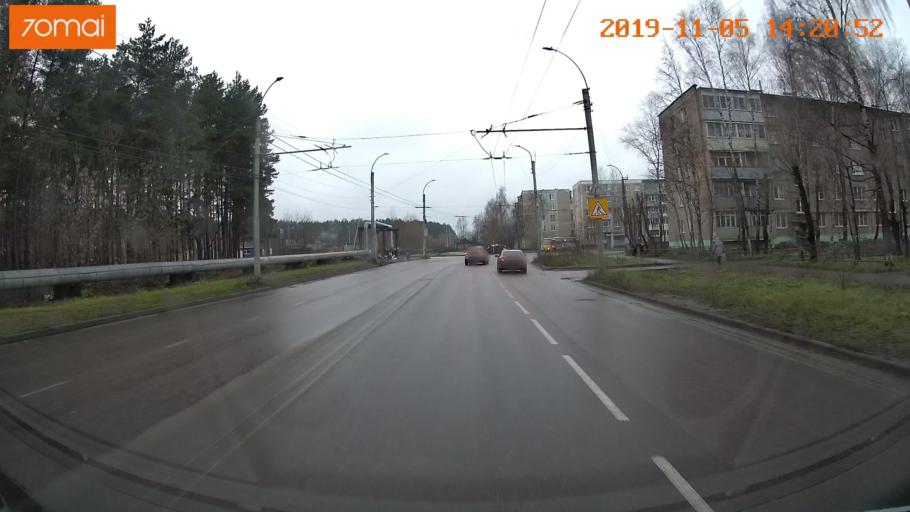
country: RU
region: Ivanovo
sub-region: Gorod Ivanovo
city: Ivanovo
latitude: 56.9570
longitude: 41.0156
